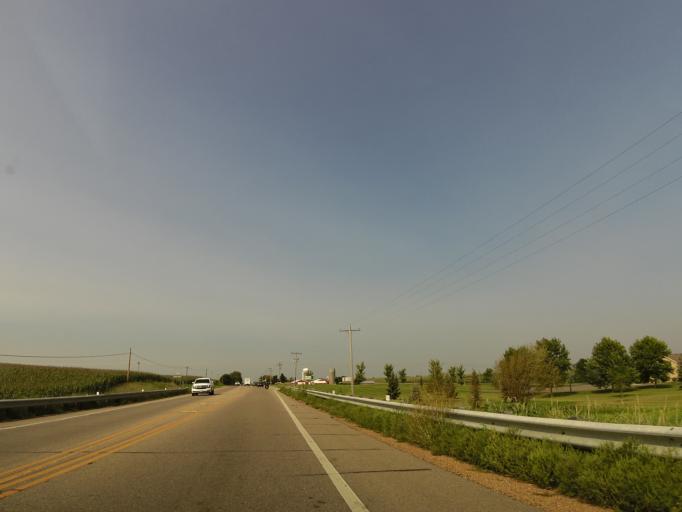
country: US
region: Minnesota
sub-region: Carver County
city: Carver
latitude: 44.7759
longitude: -93.6809
